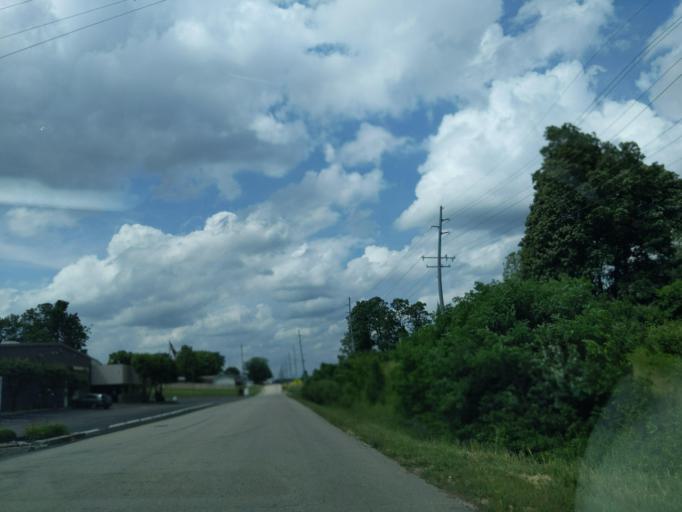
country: US
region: Indiana
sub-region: Ripley County
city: Batesville
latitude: 39.3083
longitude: -85.2083
